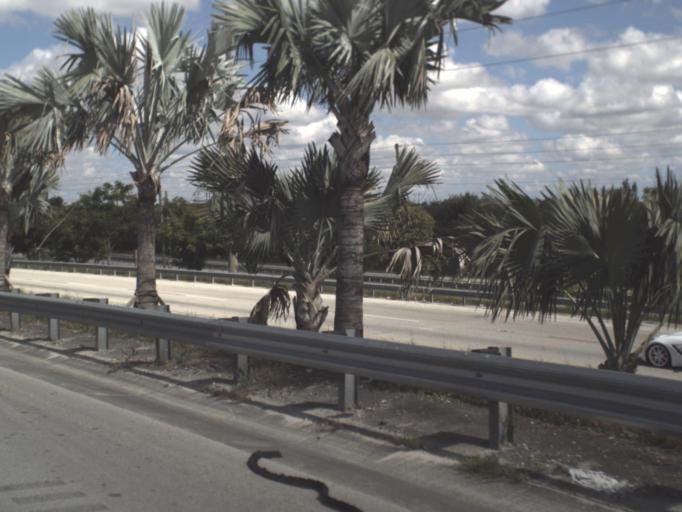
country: US
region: Florida
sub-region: Miami-Dade County
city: Doral
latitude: 25.8130
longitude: -80.3863
